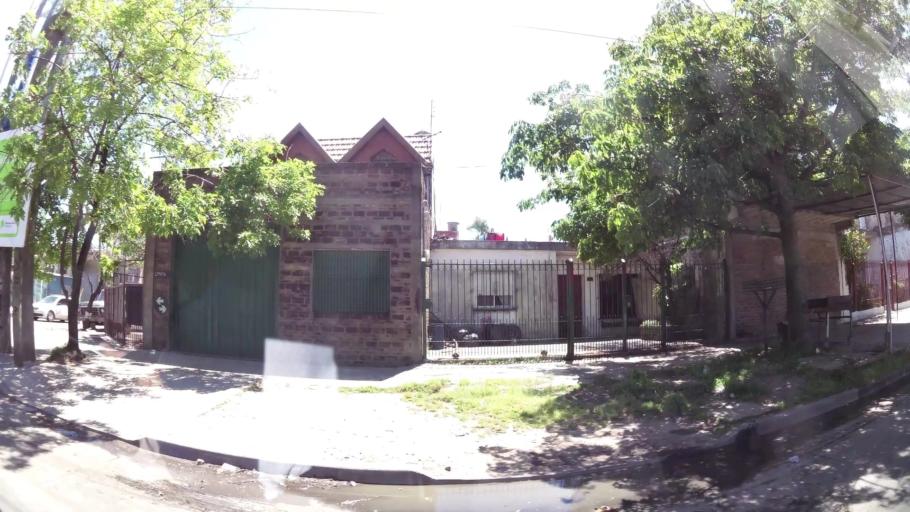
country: AR
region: Buenos Aires
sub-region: Partido de Lanus
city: Lanus
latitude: -34.7267
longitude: -58.3331
